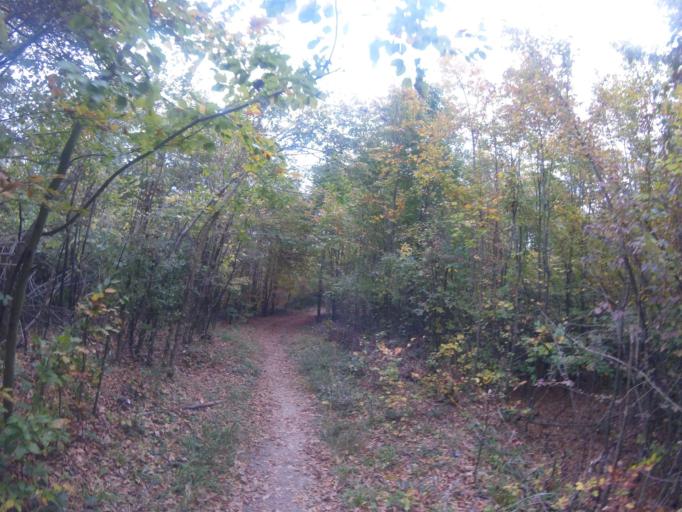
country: HU
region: Veszprem
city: Herend
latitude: 47.2629
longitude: 17.7432
